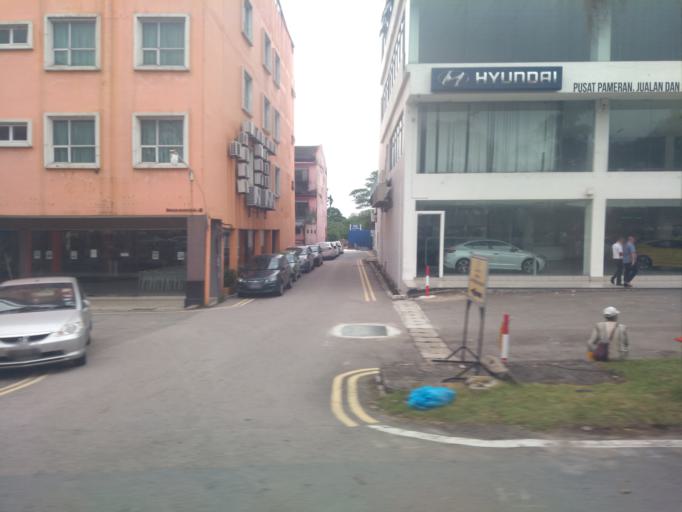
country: MY
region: Johor
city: Johor Bahru
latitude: 1.4896
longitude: 103.7113
